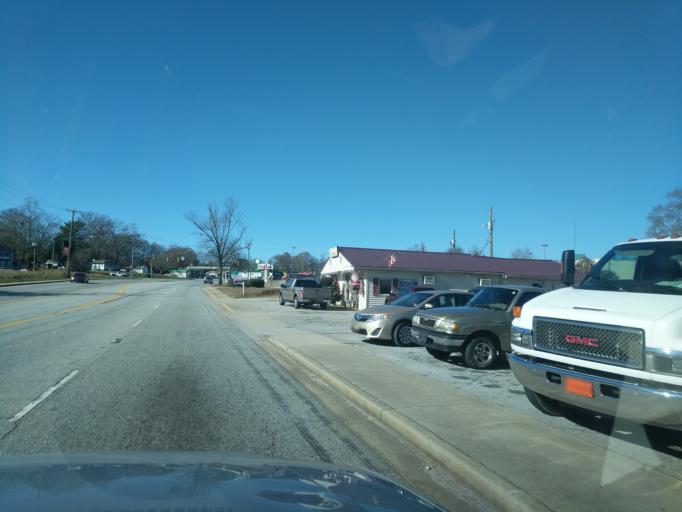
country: US
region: South Carolina
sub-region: Oconee County
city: Westminster
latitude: 34.6583
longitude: -83.0841
